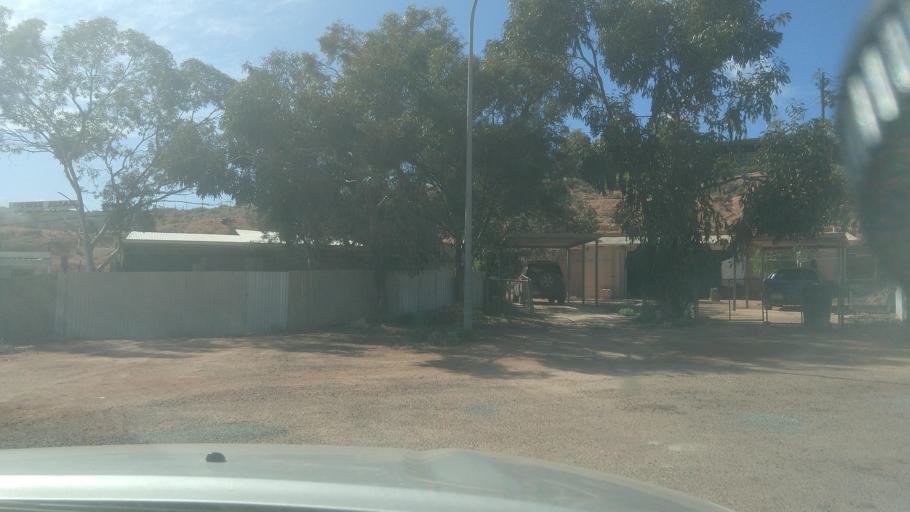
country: AU
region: South Australia
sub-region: Coober Pedy
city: Coober Pedy
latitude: -29.0116
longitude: 134.7568
